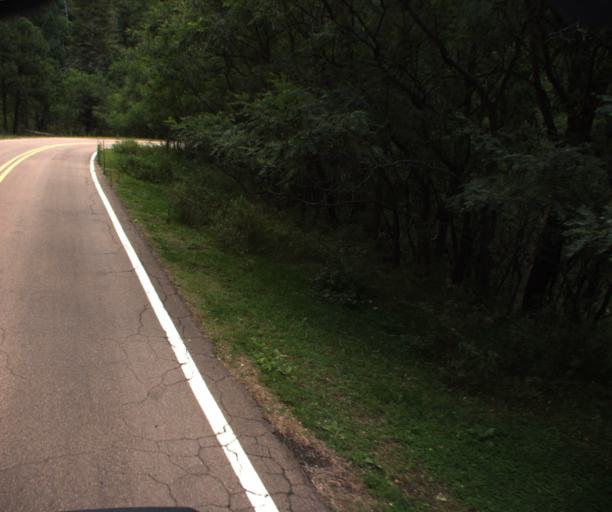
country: US
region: Arizona
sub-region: Navajo County
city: Pinetop-Lakeside
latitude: 34.0306
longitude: -109.7509
